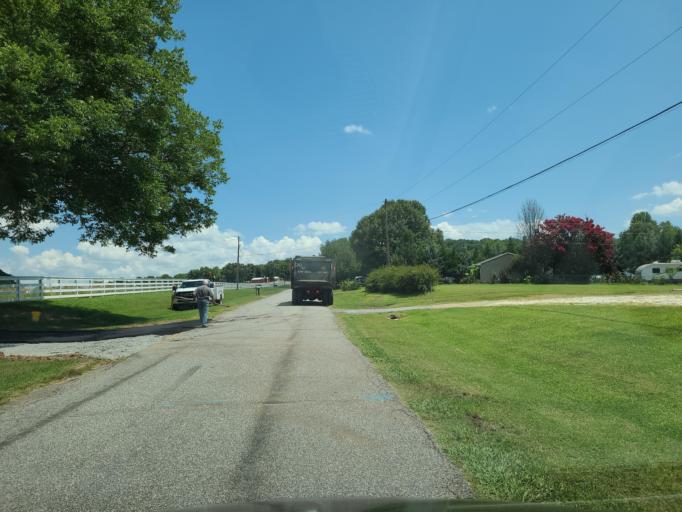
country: US
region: South Carolina
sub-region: Spartanburg County
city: Inman Mills
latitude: 35.0386
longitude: -82.1564
